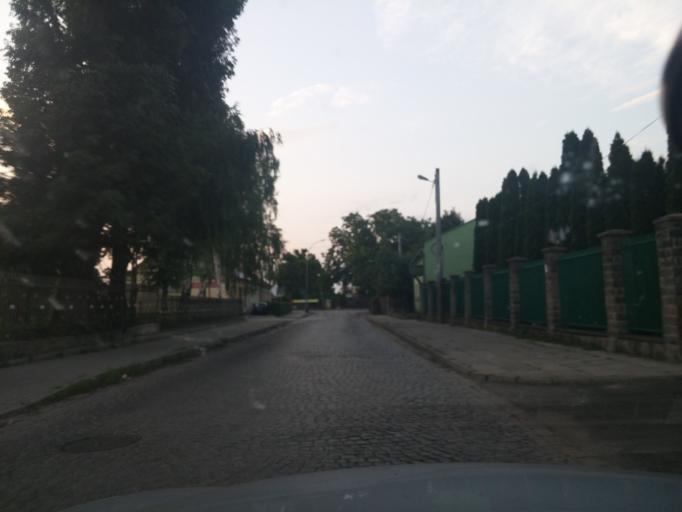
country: PL
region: Subcarpathian Voivodeship
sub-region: Przemysl
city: Przemysl
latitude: 49.7843
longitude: 22.7902
